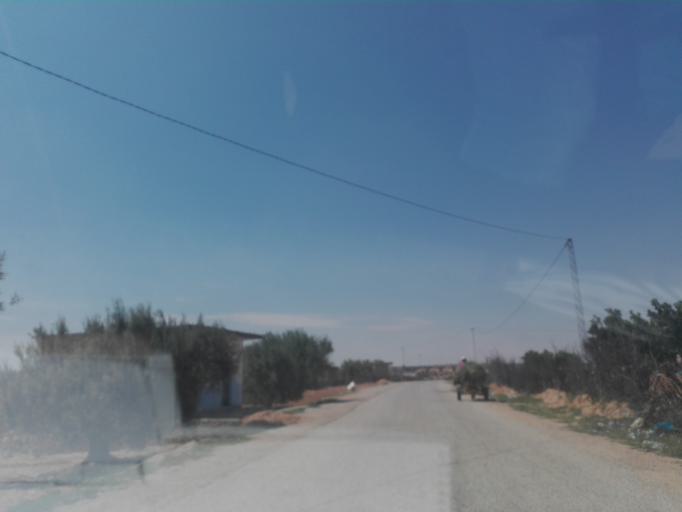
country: TN
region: Safaqis
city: Bi'r `Ali Bin Khalifah
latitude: 34.6201
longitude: 10.3650
